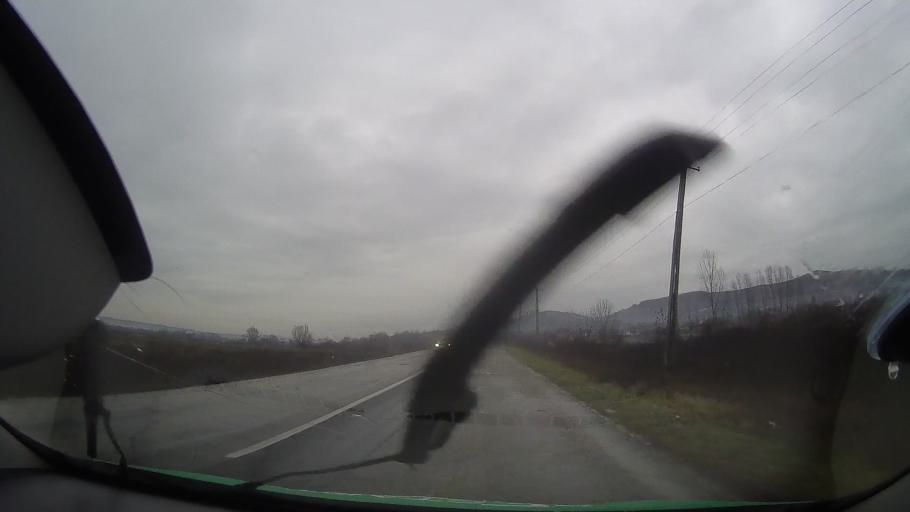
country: RO
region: Bihor
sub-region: Comuna Sambata
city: Sambata
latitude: 46.7691
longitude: 22.1863
